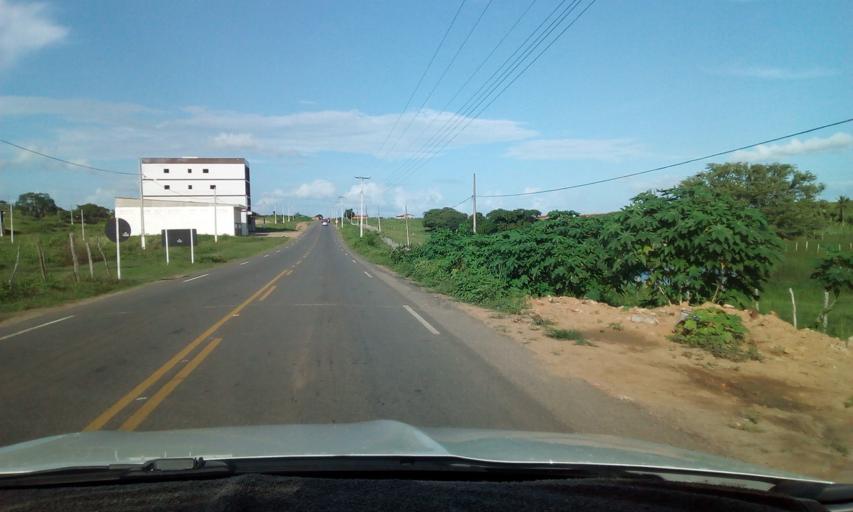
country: BR
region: Paraiba
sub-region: Guarabira
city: Guarabira
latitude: -6.8501
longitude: -35.3734
